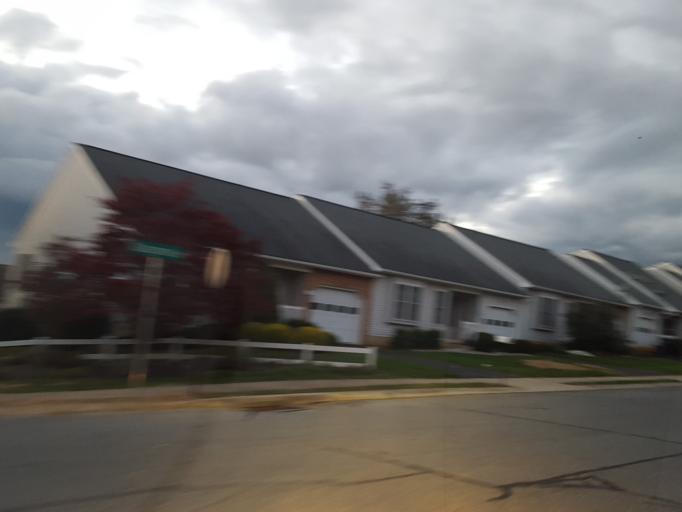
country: US
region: Pennsylvania
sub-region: Lancaster County
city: Millersville
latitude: 39.9954
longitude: -76.3718
